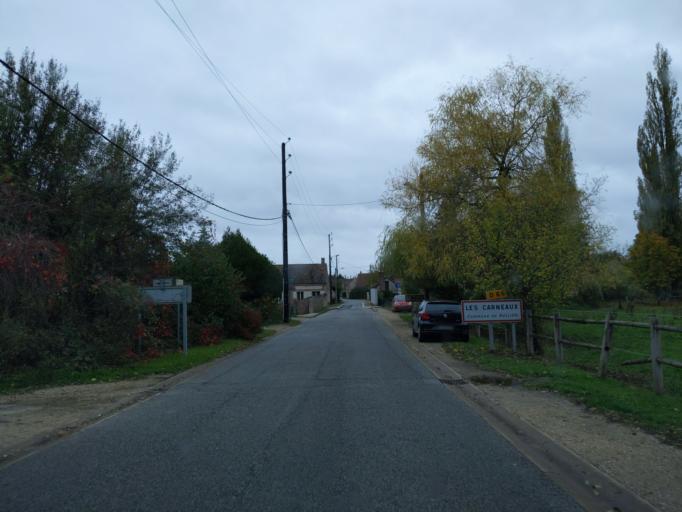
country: FR
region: Ile-de-France
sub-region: Departement des Yvelines
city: Bullion
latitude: 48.6221
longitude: 1.9919
